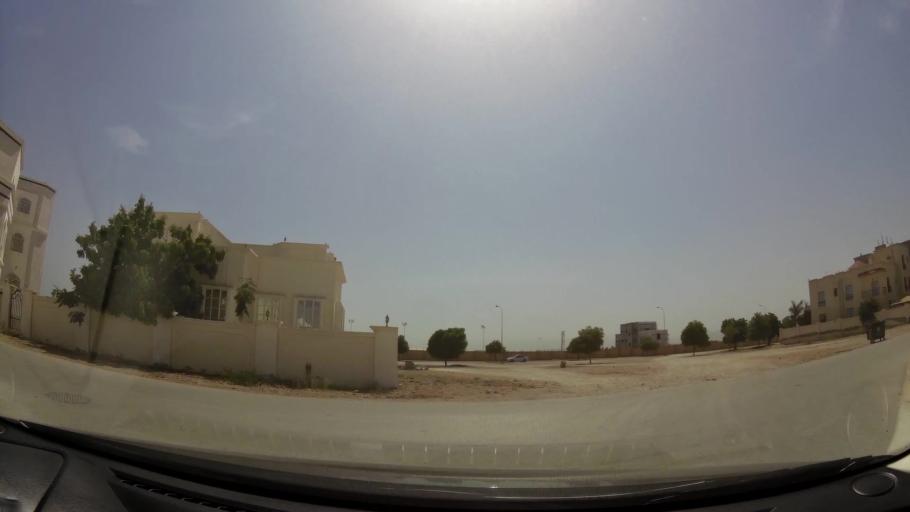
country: OM
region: Zufar
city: Salalah
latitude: 17.0410
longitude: 54.1495
